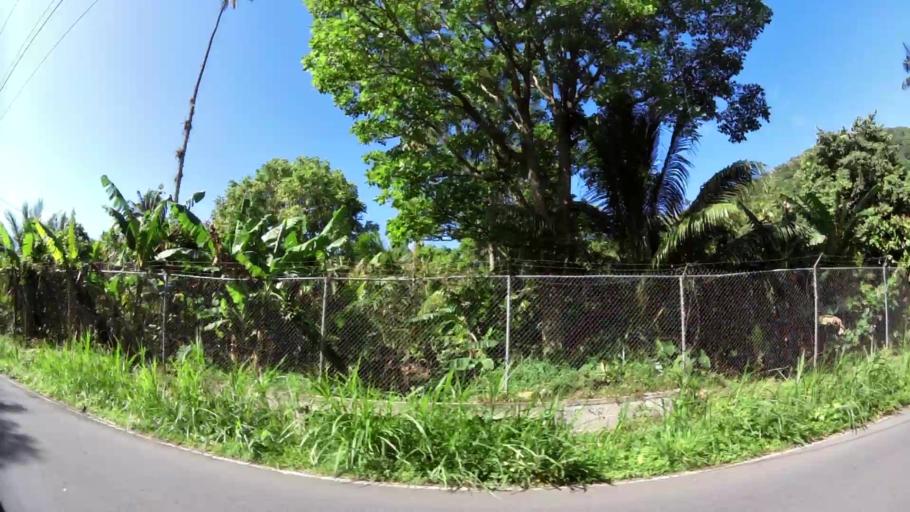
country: LC
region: Soufriere
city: Soufriere
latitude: 13.8226
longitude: -61.0483
